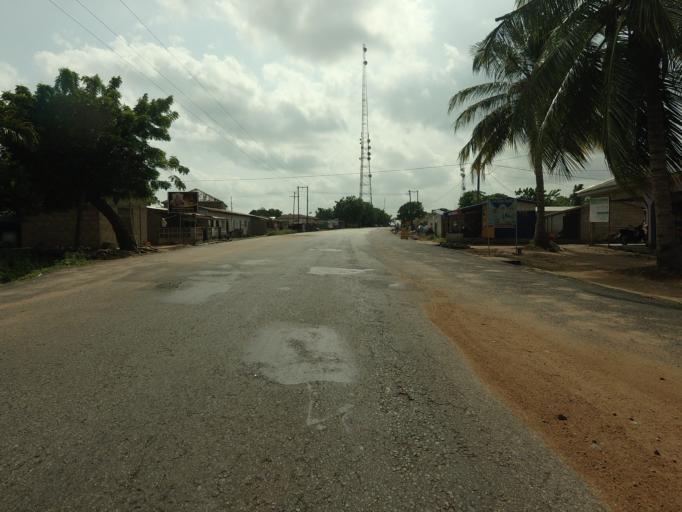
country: GH
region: Volta
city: Ho
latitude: 6.4158
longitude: 0.7460
